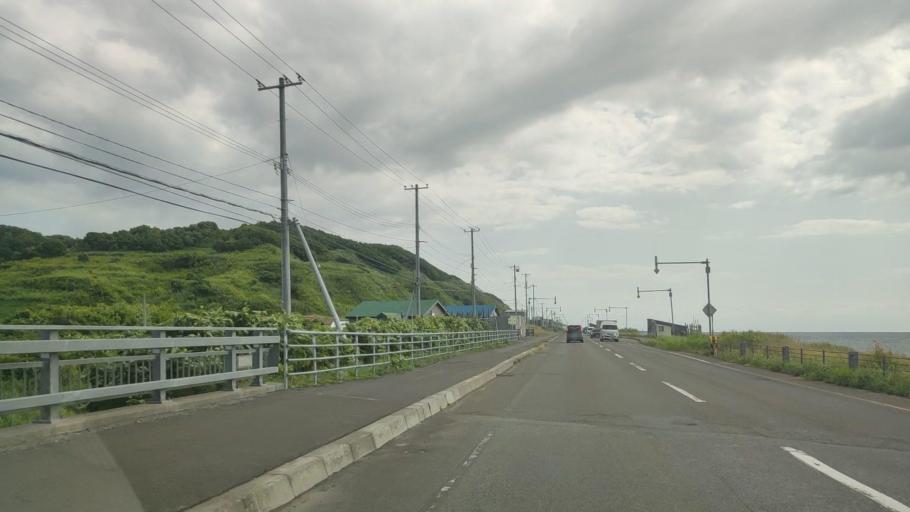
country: JP
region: Hokkaido
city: Rumoi
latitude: 44.1815
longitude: 141.6588
